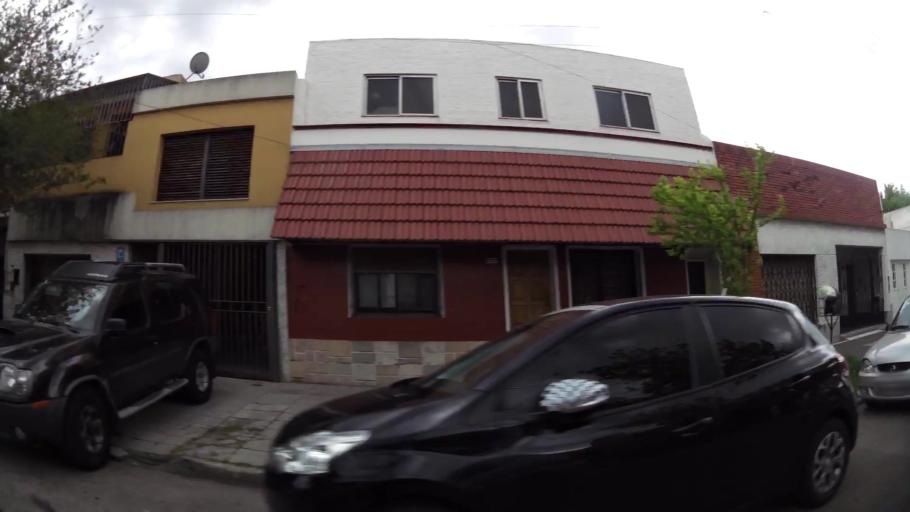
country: AR
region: Buenos Aires
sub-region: Partido de Lanus
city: Lanus
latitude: -34.6870
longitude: -58.3902
